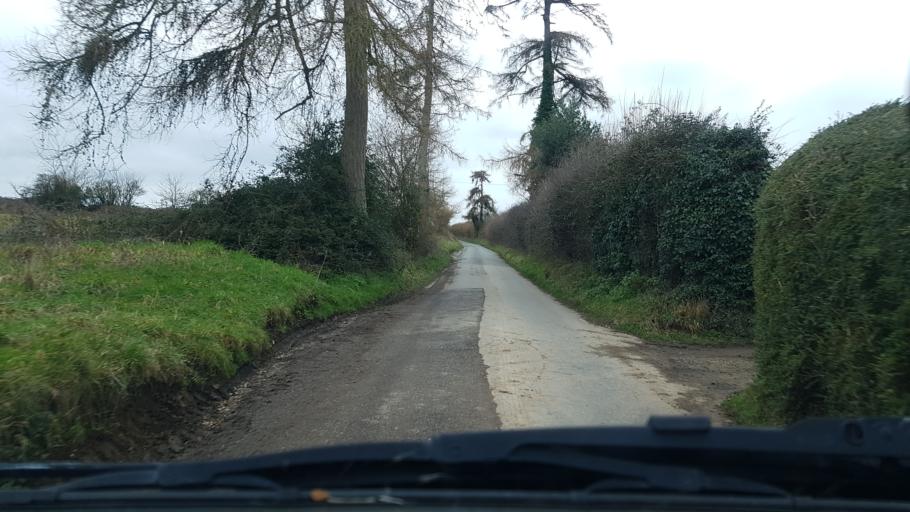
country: GB
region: England
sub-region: Wiltshire
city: Shalbourne
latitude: 51.3301
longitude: -1.5651
